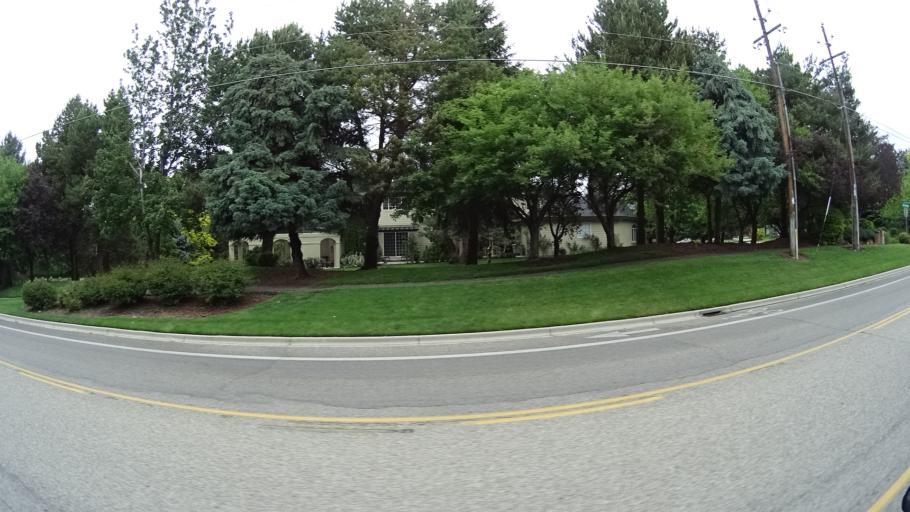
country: US
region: Idaho
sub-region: Ada County
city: Eagle
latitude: 43.7065
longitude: -116.3314
